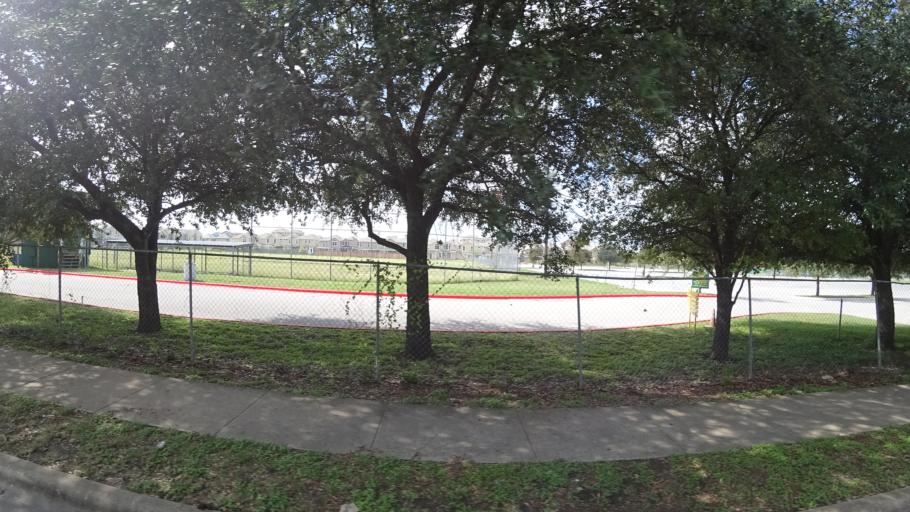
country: US
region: Texas
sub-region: Travis County
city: Austin
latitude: 30.3458
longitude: -97.7189
